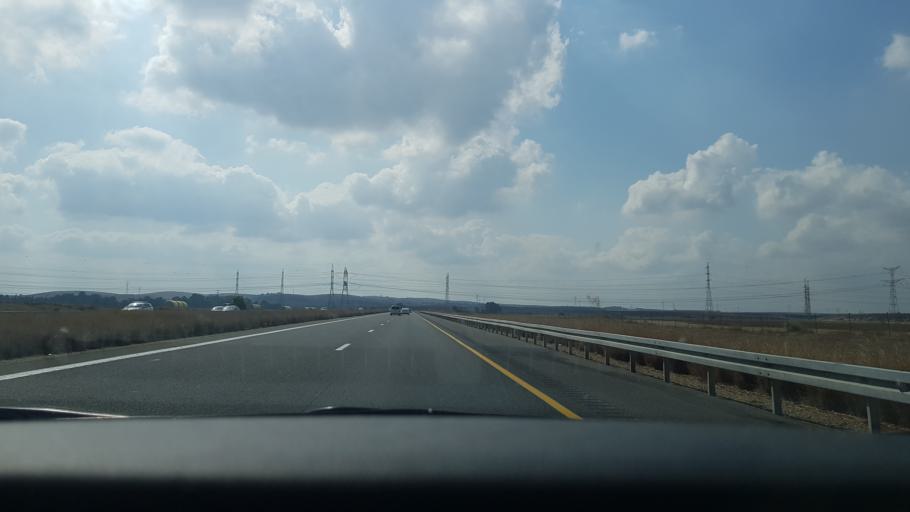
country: IL
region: Central District
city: Bene 'Ayish
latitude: 31.7171
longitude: 34.8204
